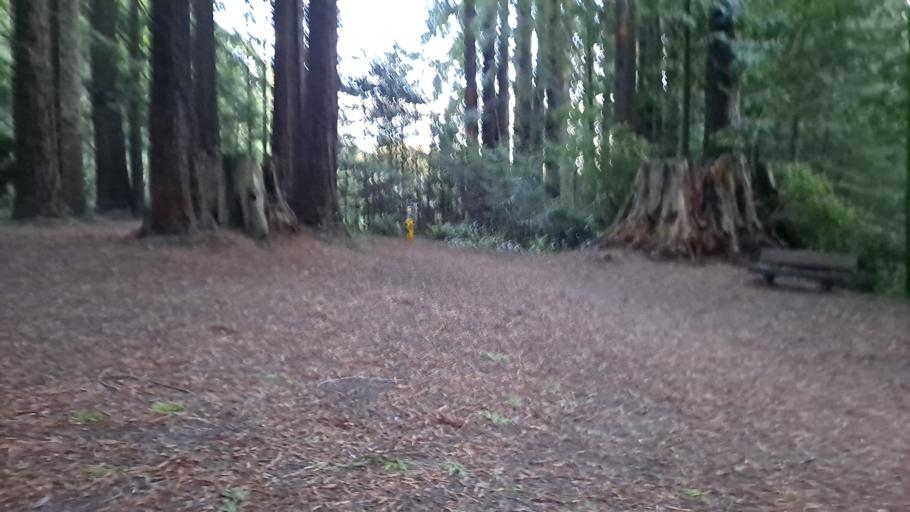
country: US
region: California
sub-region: Humboldt County
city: Fortuna
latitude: 40.6013
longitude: -124.1453
